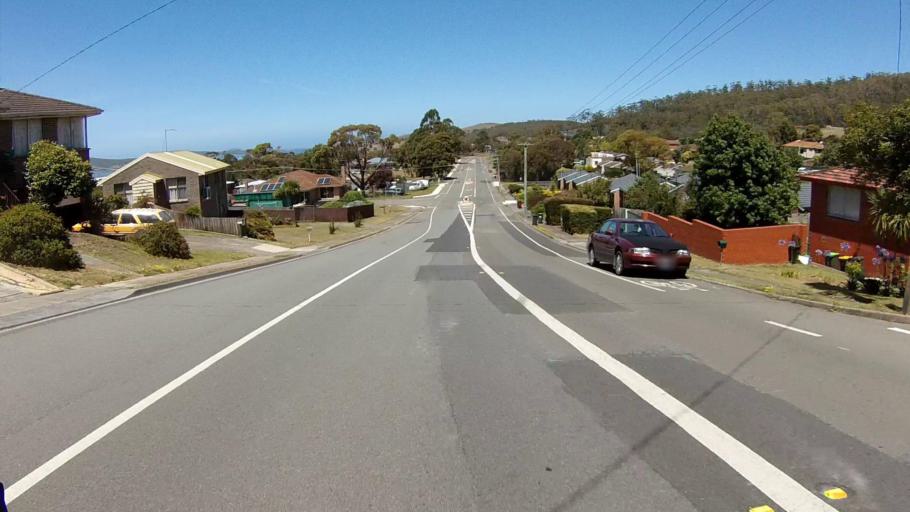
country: AU
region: Tasmania
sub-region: Clarence
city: Rokeby
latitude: -42.8931
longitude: 147.4314
